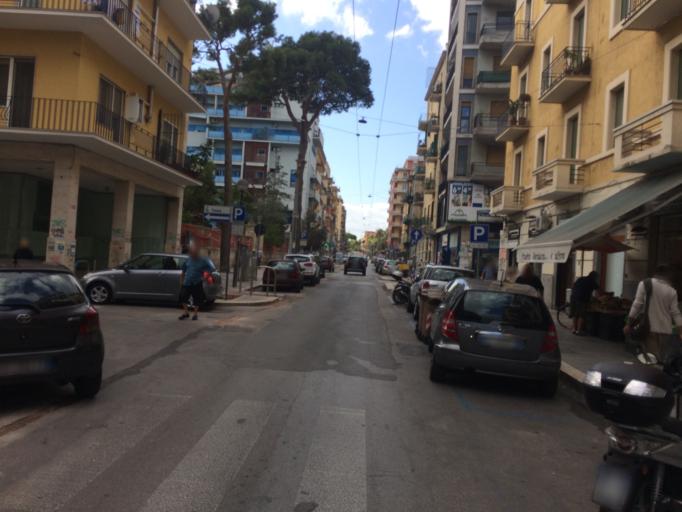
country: IT
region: Apulia
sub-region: Provincia di Bari
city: Bari
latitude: 41.1090
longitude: 16.8719
